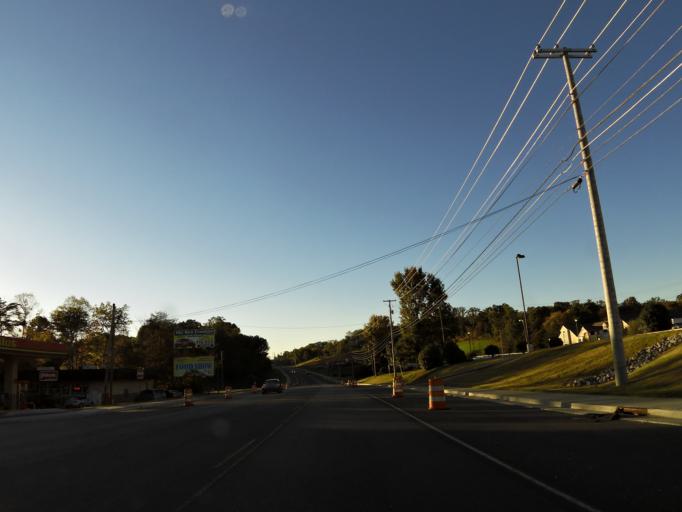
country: US
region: Tennessee
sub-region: Knox County
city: Knoxville
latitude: 35.9802
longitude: -84.0165
